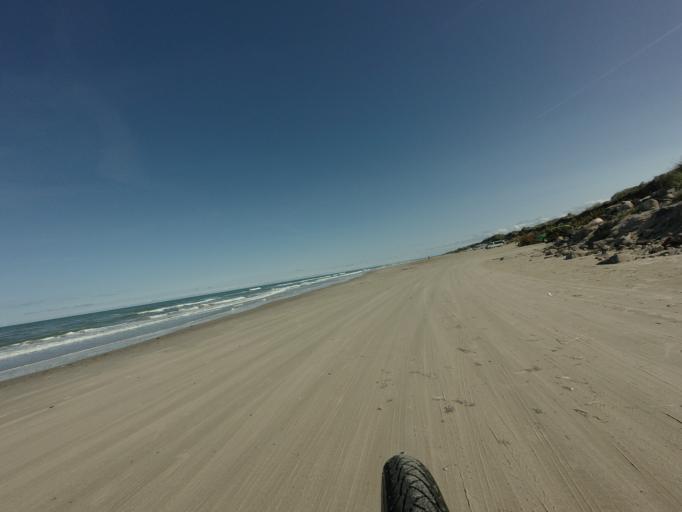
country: DK
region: North Denmark
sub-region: Hjorring Kommune
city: Hirtshals
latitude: 57.5894
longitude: 10.0282
